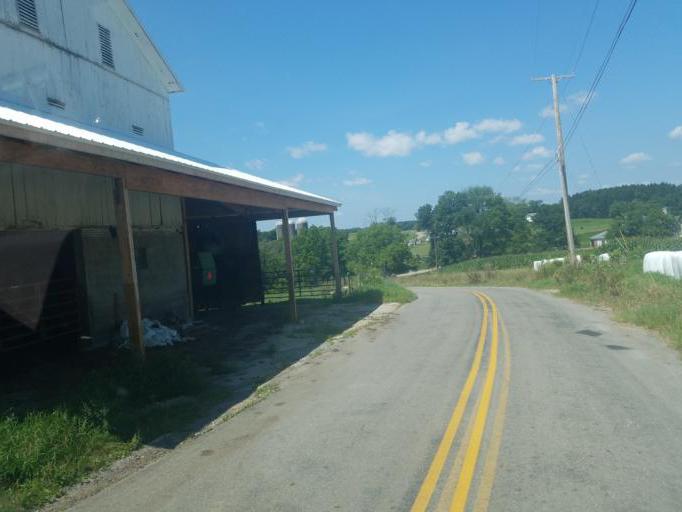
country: US
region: Pennsylvania
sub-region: Clarion County
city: Knox
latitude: 41.1970
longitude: -79.5515
